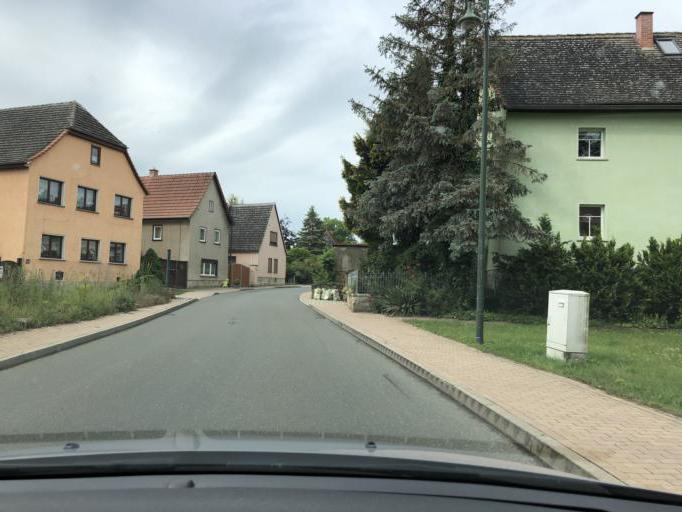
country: DE
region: Thuringia
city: Rannstedt
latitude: 51.0994
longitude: 11.5304
